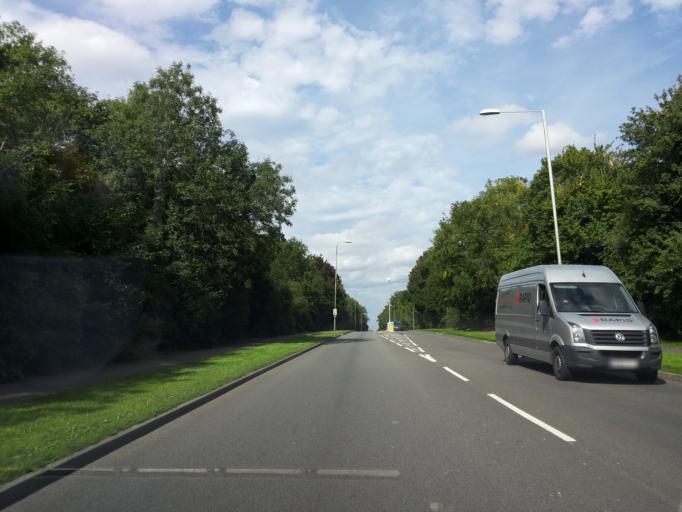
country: GB
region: England
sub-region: Greater London
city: Orpington
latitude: 51.3516
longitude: 0.0880
